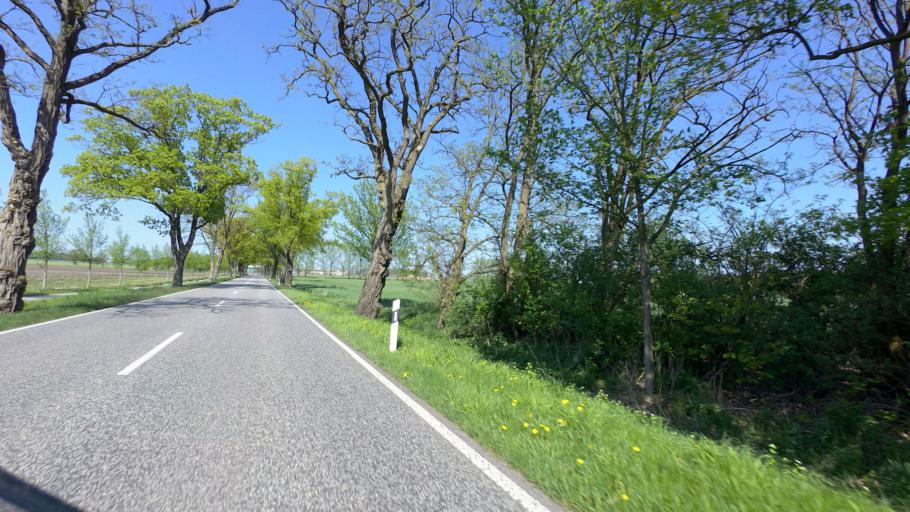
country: DE
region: Brandenburg
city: Beeskow
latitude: 52.1458
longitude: 14.2604
